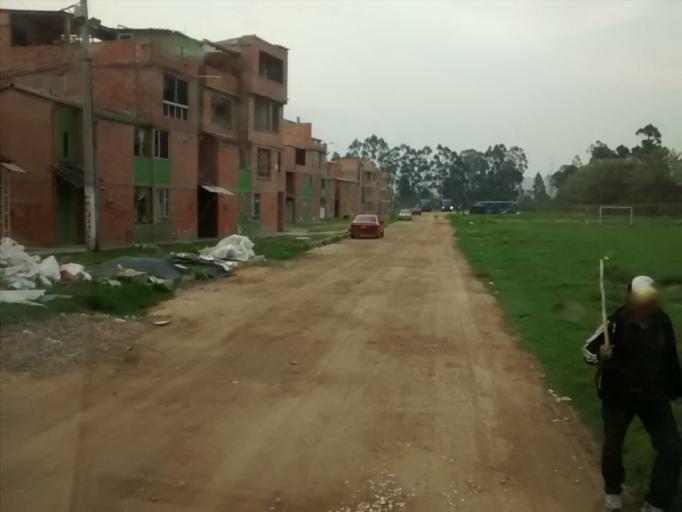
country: CO
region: Cundinamarca
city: Cota
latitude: 4.7593
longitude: -74.1135
